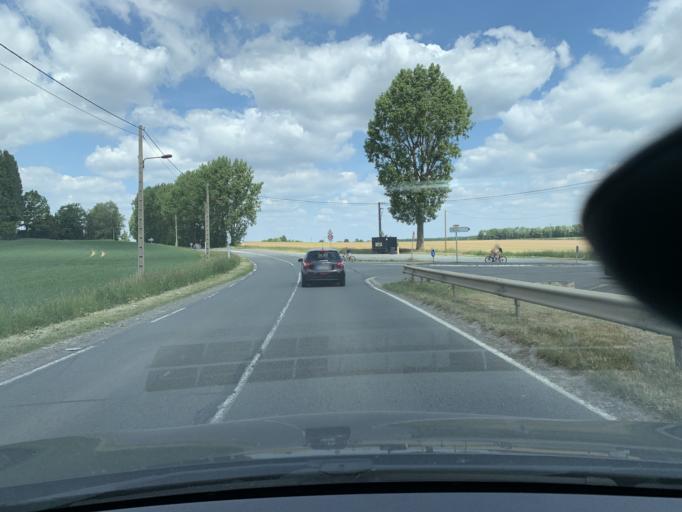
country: FR
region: Nord-Pas-de-Calais
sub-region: Departement du Nord
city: Goeulzin
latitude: 50.3080
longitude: 3.0988
